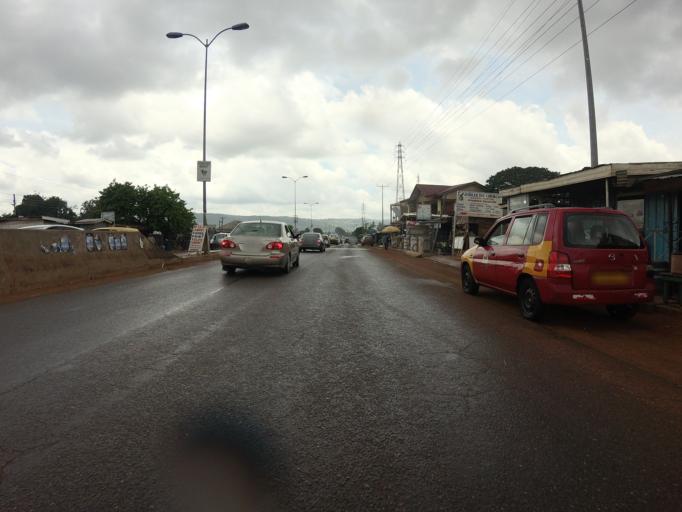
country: GH
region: Greater Accra
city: Medina Estates
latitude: 5.7428
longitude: -0.1767
